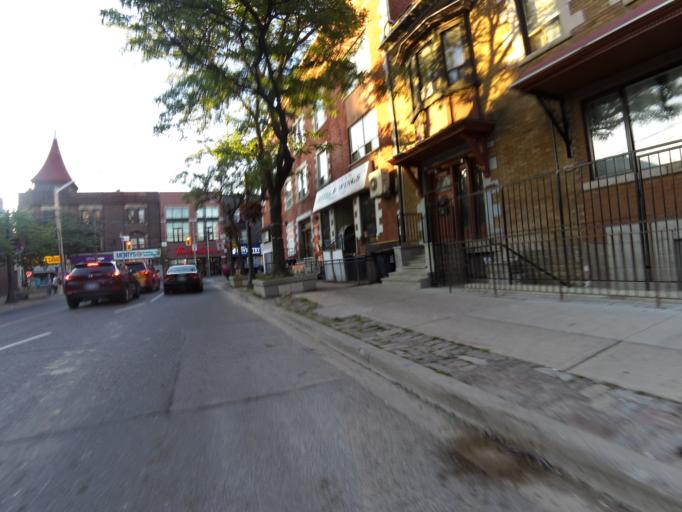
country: CA
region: Ontario
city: Toronto
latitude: 43.6401
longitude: -79.4371
